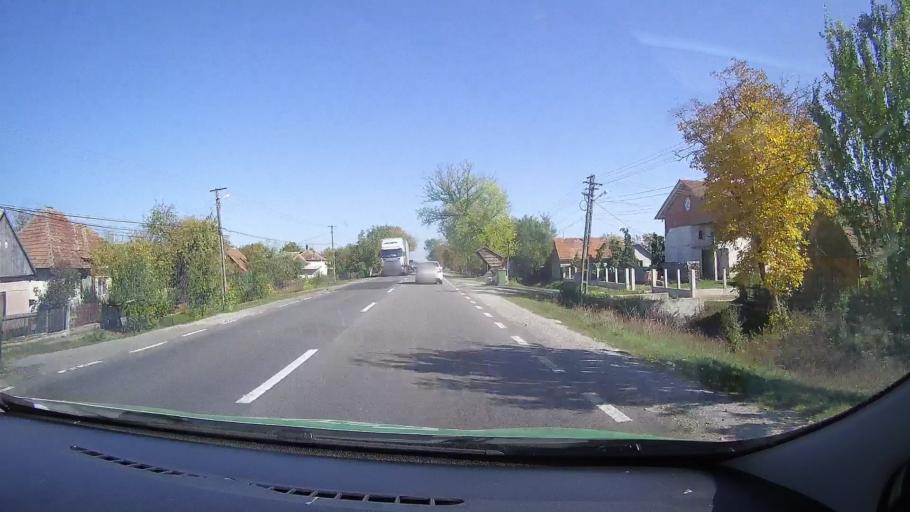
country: RO
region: Satu Mare
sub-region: Comuna Doba
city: Doba
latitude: 47.7304
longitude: 22.6853
